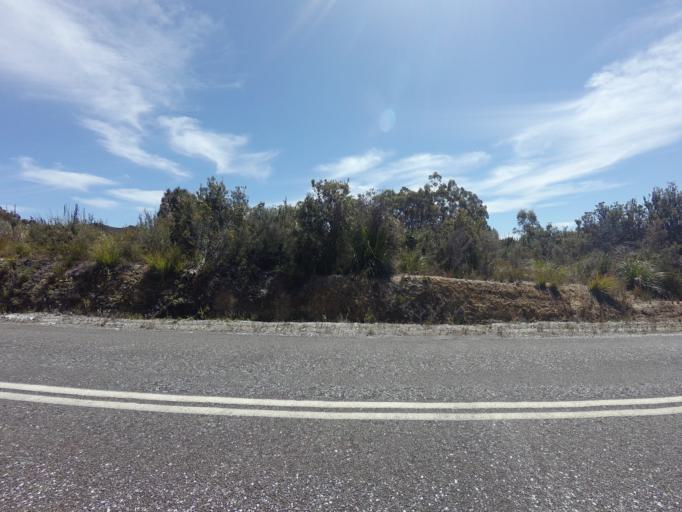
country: AU
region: Tasmania
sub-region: Huon Valley
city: Geeveston
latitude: -42.8361
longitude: 146.1440
